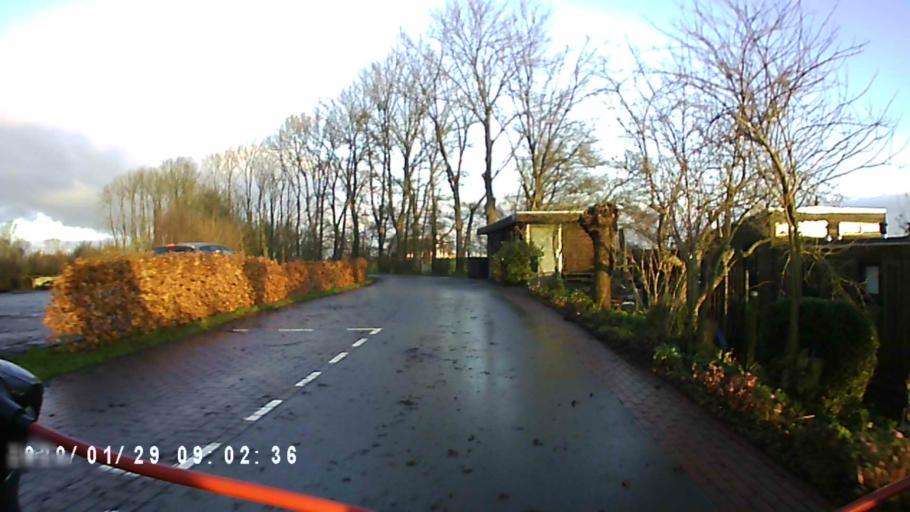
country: NL
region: Groningen
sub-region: Gemeente Winsum
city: Winsum
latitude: 53.3176
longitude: 6.4692
